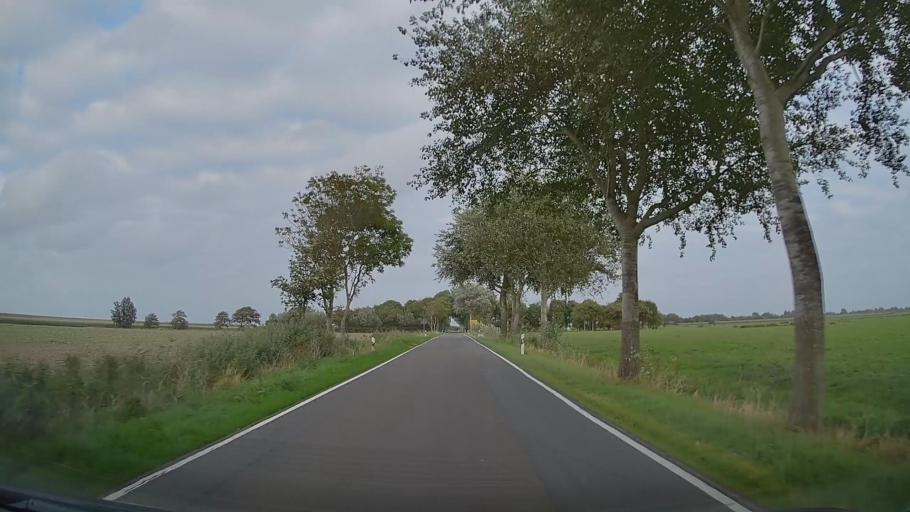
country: DE
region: Schleswig-Holstein
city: Osterhever
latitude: 54.4038
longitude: 8.8132
